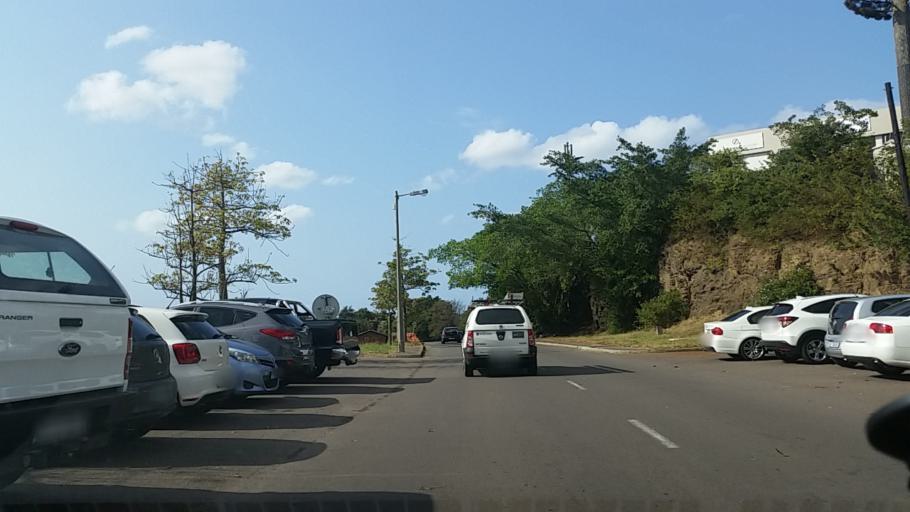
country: ZA
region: KwaZulu-Natal
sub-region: eThekwini Metropolitan Municipality
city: Berea
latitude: -29.8305
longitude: 30.9522
